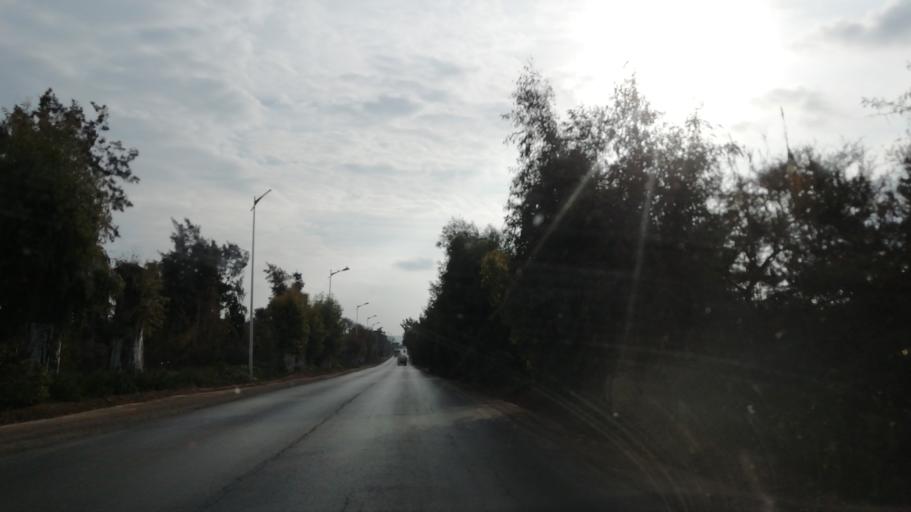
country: DZ
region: Mostaganem
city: Mostaganem
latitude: 35.8723
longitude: 0.0773
